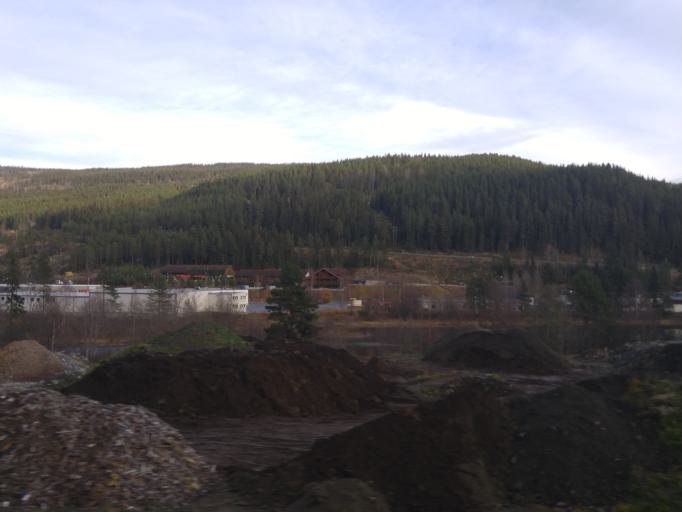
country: NO
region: Oppland
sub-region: Nord-Aurdal
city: Fagernes
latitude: 60.9995
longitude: 9.2102
